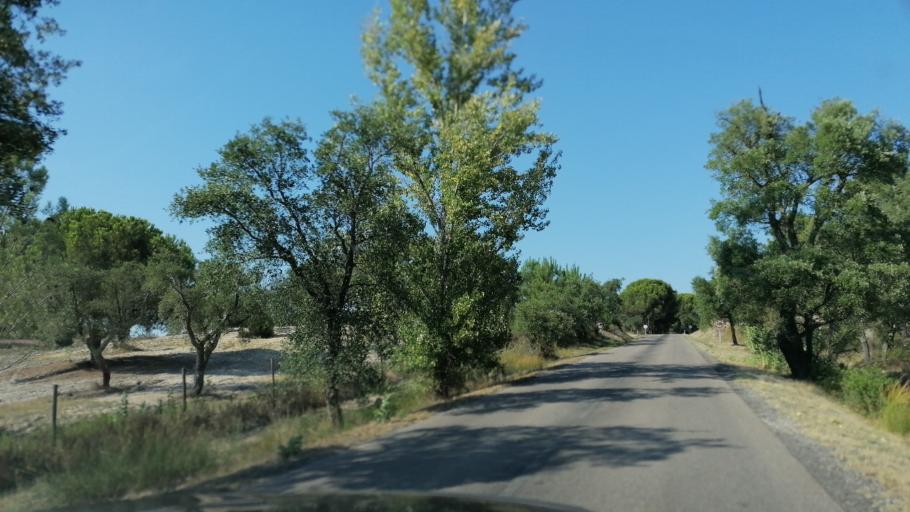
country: PT
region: Santarem
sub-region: Coruche
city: Coruche
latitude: 38.8099
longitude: -8.5770
